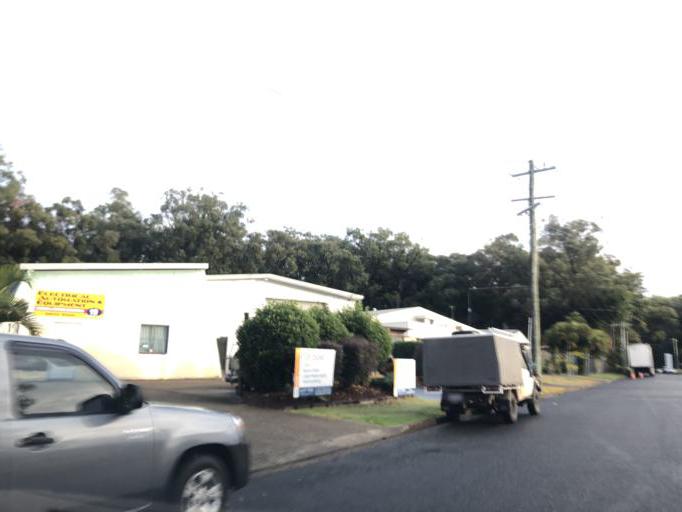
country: AU
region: New South Wales
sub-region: Coffs Harbour
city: Coffs Harbour
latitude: -30.2903
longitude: 153.1278
